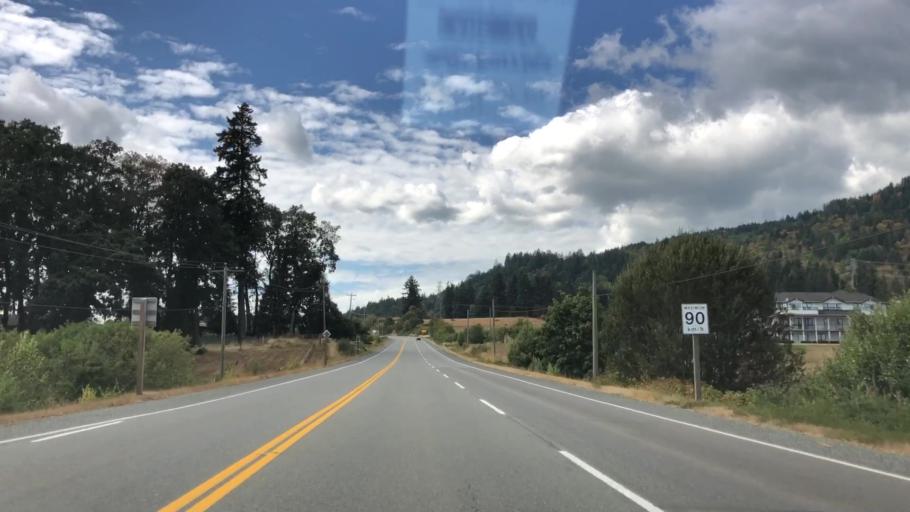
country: CA
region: British Columbia
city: Duncan
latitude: 48.8142
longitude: -123.7375
